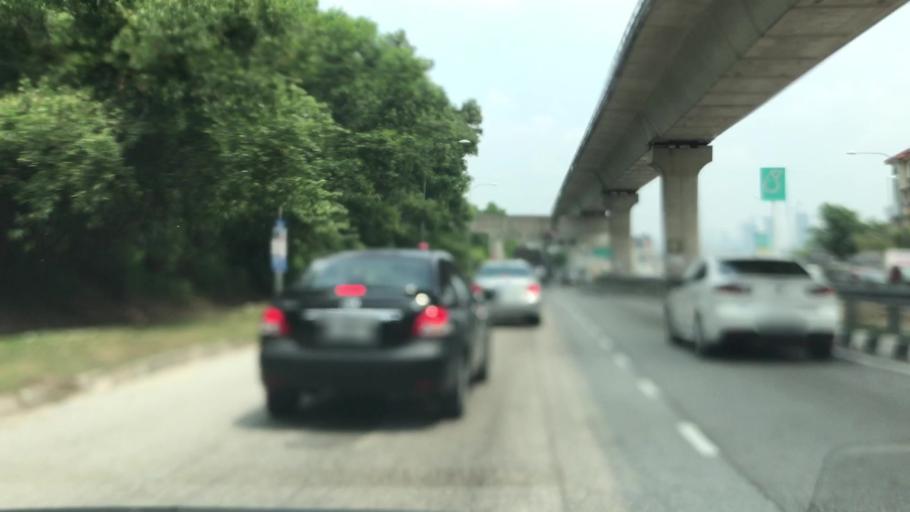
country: MY
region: Selangor
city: Subang Jaya
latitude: 3.0496
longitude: 101.6302
